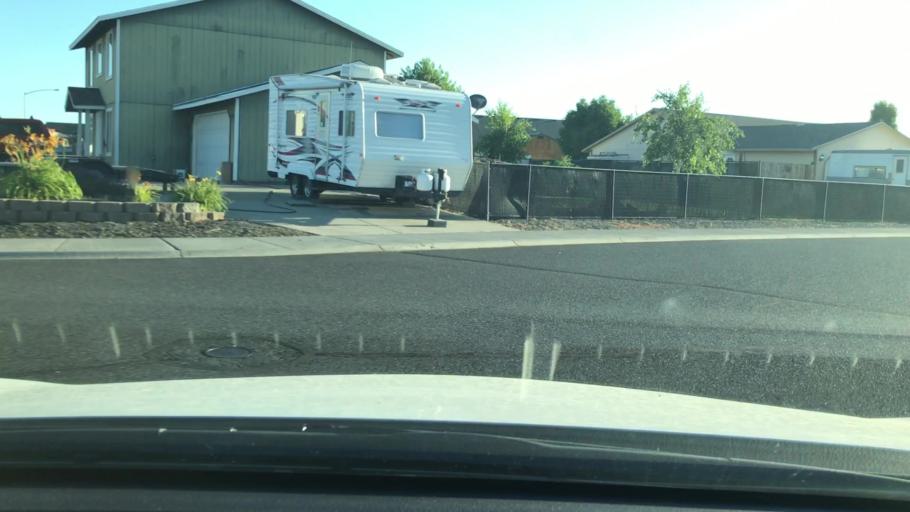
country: US
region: Washington
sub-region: Grant County
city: Moses Lake
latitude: 47.1197
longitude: -119.2556
